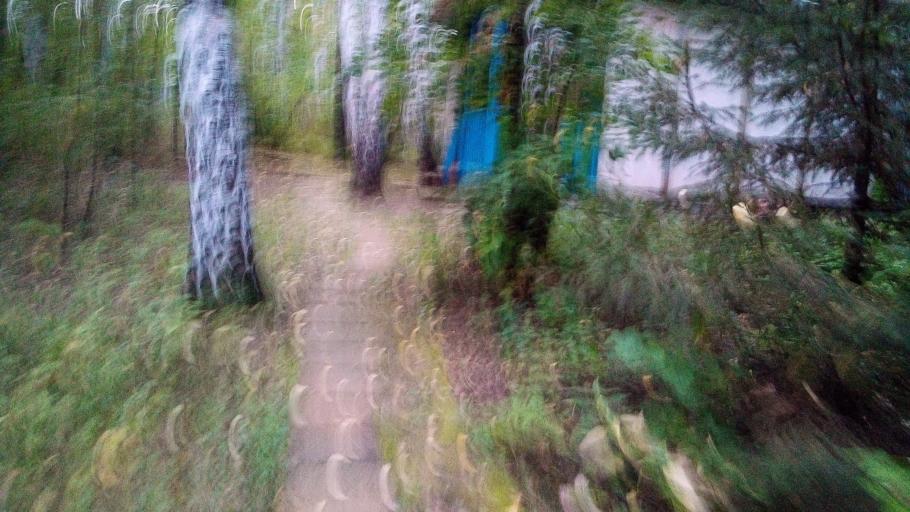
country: RU
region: Chelyabinsk
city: Tayginka
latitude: 55.4774
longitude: 60.4990
